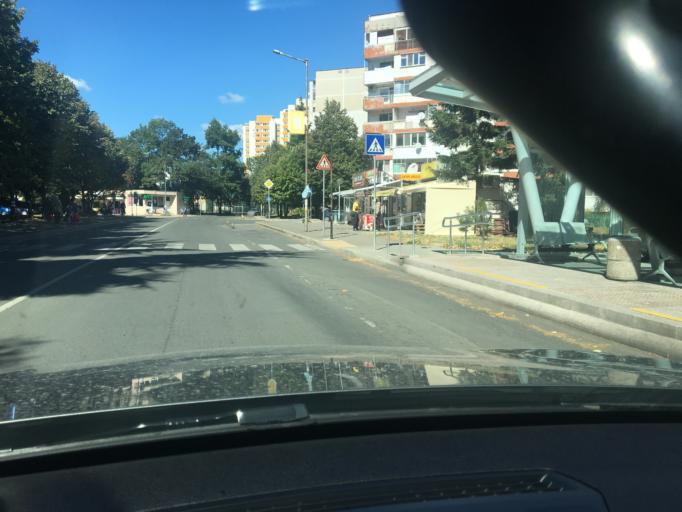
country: BG
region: Burgas
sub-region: Obshtina Burgas
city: Burgas
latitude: 42.5274
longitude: 27.4644
